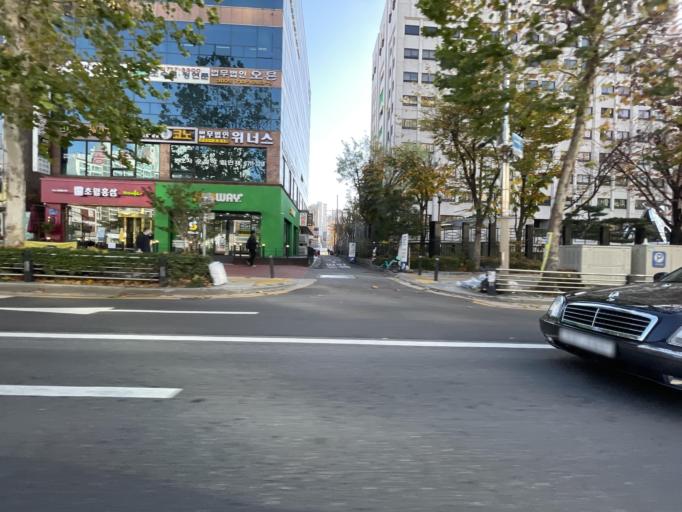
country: KR
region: Seoul
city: Seoul
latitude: 37.5501
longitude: 126.9552
